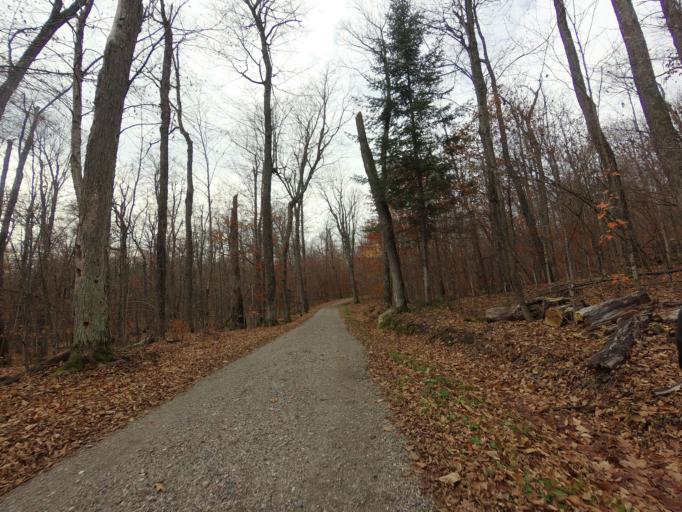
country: CA
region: Quebec
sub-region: Outaouais
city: Wakefield
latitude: 45.5408
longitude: -75.9473
